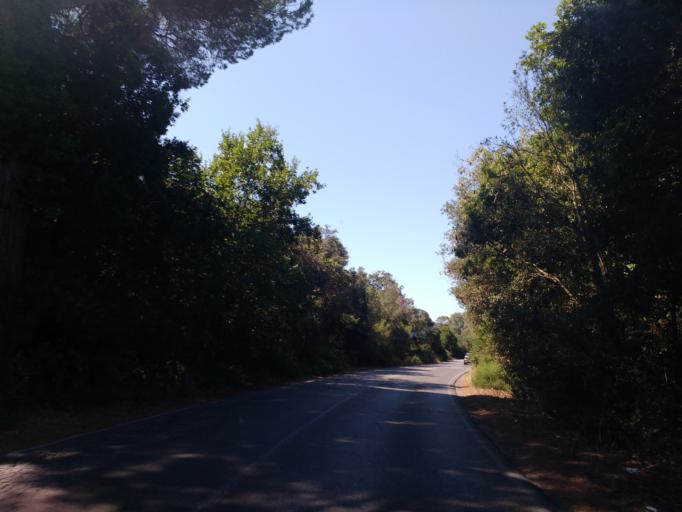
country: IT
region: Latium
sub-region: Citta metropolitana di Roma Capitale
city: Acilia-Castel Fusano-Ostia Antica
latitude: 41.7094
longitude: 12.3573
